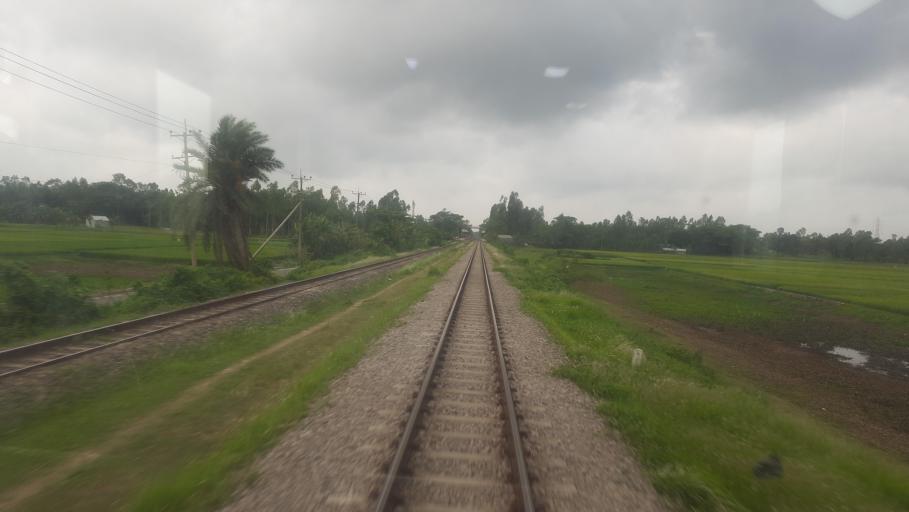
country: BD
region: Dhaka
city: Narsingdi
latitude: 23.9720
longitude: 90.8283
